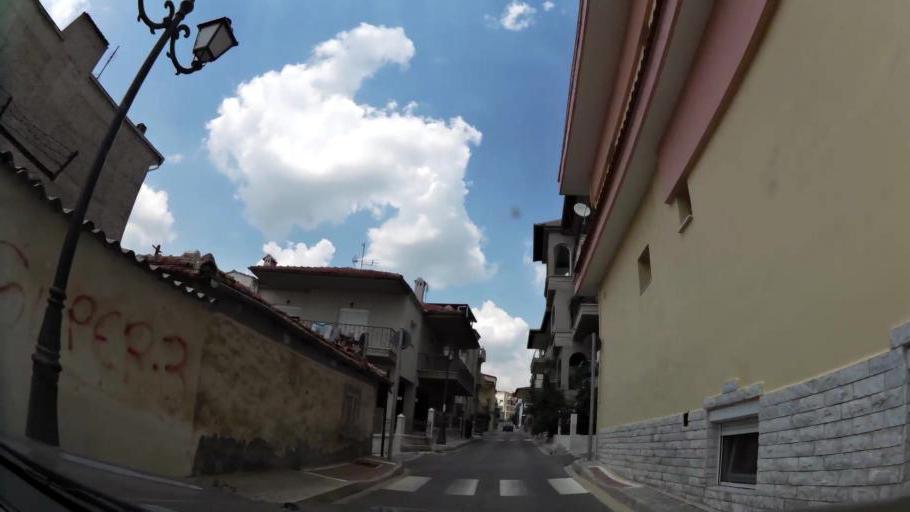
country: GR
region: West Macedonia
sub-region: Nomos Kozanis
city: Kozani
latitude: 40.3066
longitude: 21.7920
